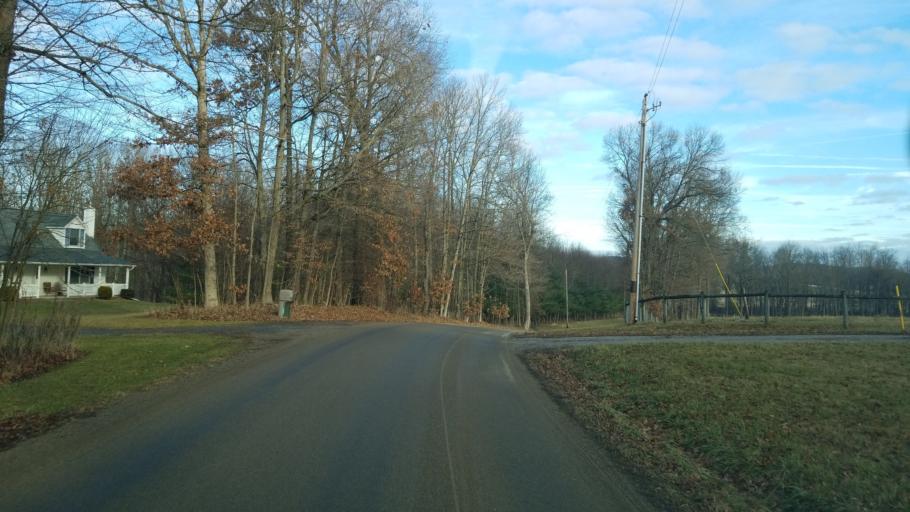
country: US
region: Ohio
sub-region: Knox County
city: Gambier
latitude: 40.3316
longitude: -82.3824
